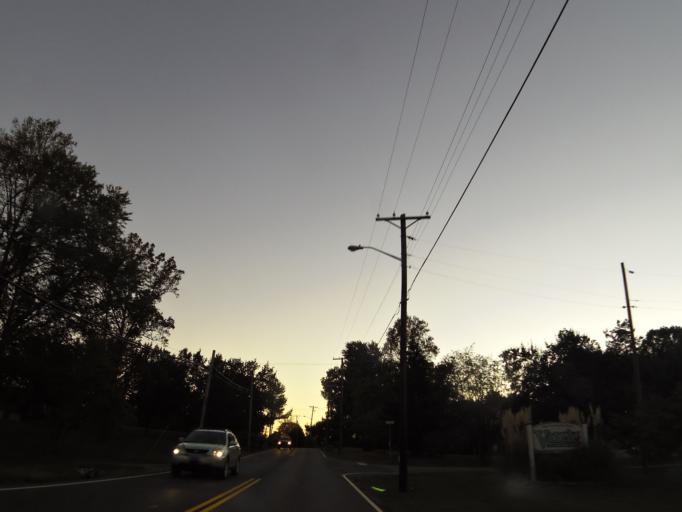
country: US
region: Tennessee
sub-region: Knox County
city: Knoxville
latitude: 36.0444
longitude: -83.9056
